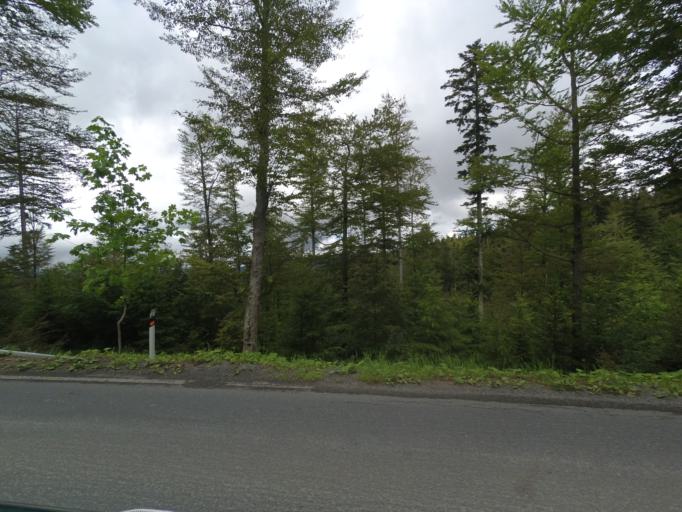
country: CZ
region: Plzensky
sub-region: Okres Klatovy
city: Zelezna Ruda
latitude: 49.1785
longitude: 13.2347
